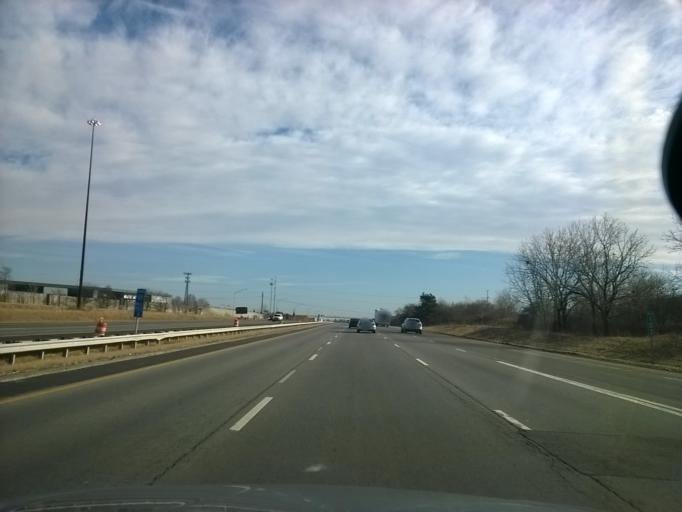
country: US
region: Indiana
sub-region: Marion County
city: Southport
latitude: 39.6641
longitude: -86.0876
